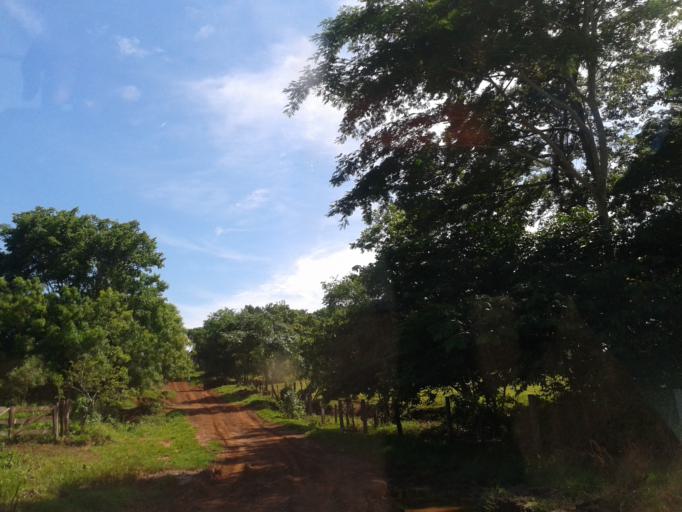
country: BR
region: Minas Gerais
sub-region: Santa Vitoria
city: Santa Vitoria
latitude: -19.0868
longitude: -50.0172
